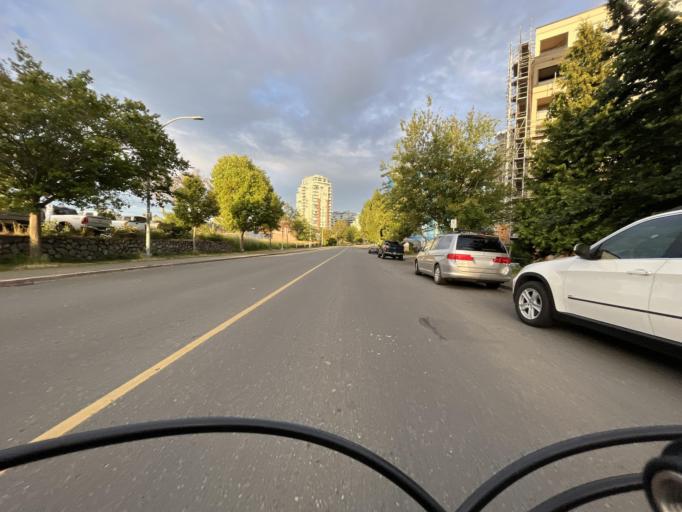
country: CA
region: British Columbia
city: Victoria
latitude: 48.4292
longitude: -123.3839
